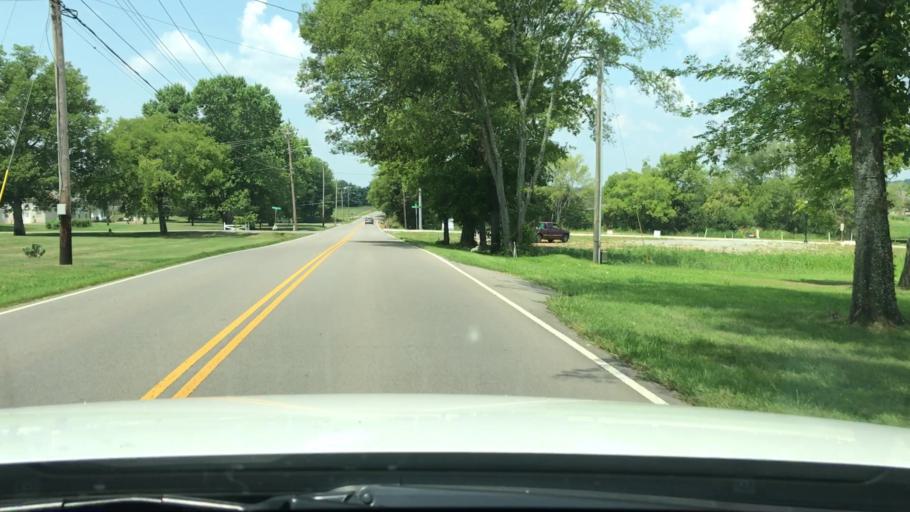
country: US
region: Tennessee
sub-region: Sumner County
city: Gallatin
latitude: 36.3600
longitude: -86.4540
